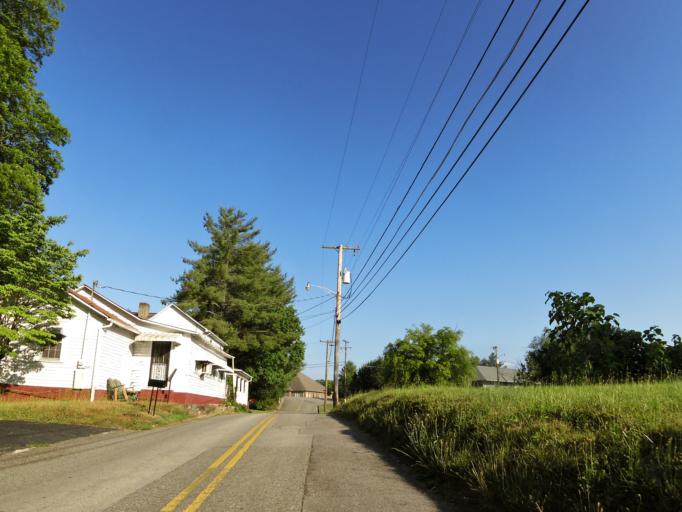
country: US
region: Tennessee
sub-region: Blount County
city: Maryville
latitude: 35.7600
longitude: -83.9652
